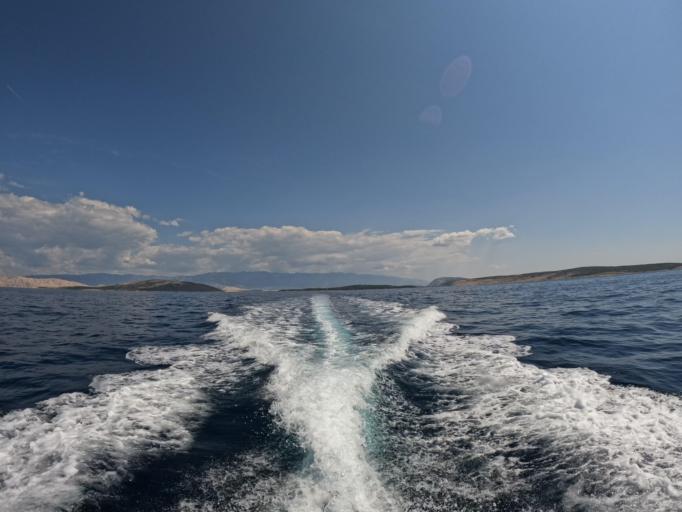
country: HR
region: Primorsko-Goranska
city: Lopar
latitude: 44.8652
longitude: 14.6849
